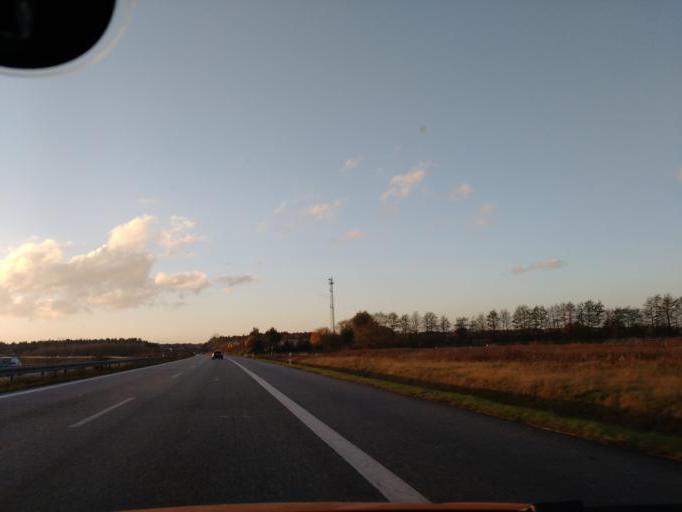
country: DE
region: Mecklenburg-Vorpommern
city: Stralendorf
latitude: 53.4839
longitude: 11.2806
